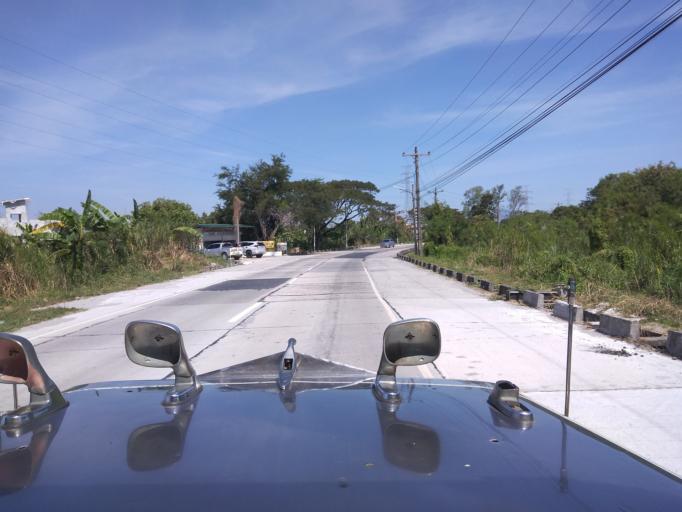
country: PH
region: Central Luzon
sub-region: Province of Pampanga
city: Bacolor
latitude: 15.0089
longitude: 120.6605
